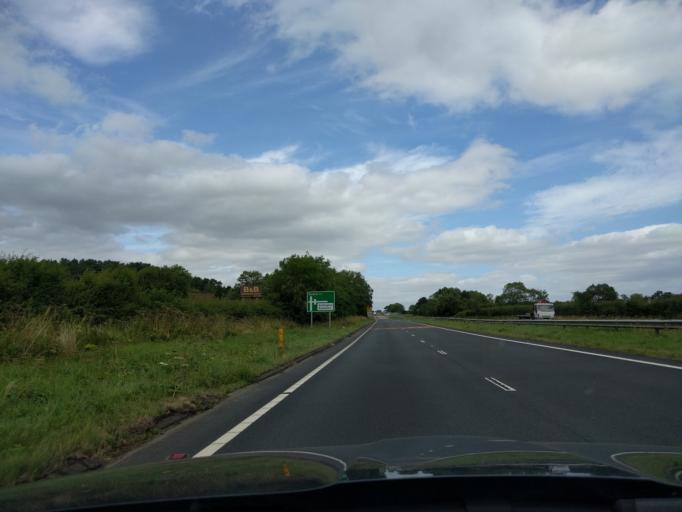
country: GB
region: England
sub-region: Northumberland
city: Felton
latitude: 55.3264
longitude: -1.7248
